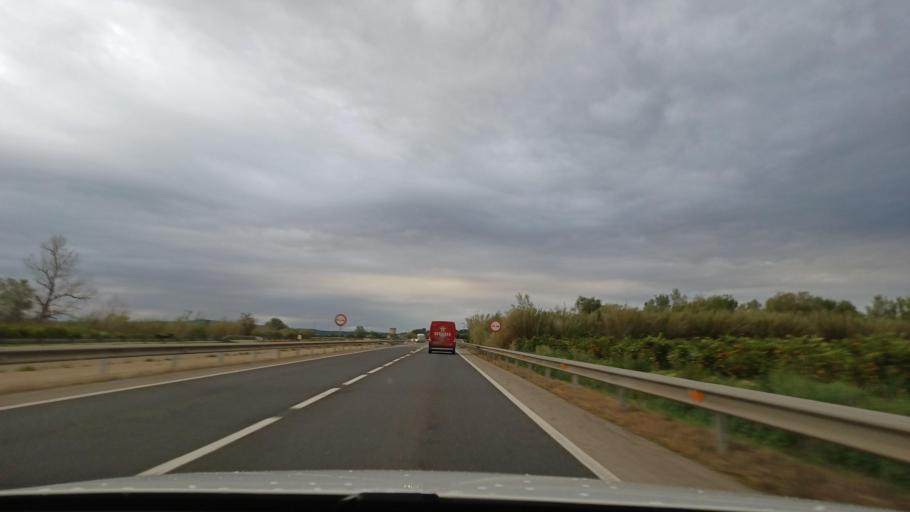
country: ES
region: Catalonia
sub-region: Provincia de Tarragona
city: Masdenverge
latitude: 40.7534
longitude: 0.5426
